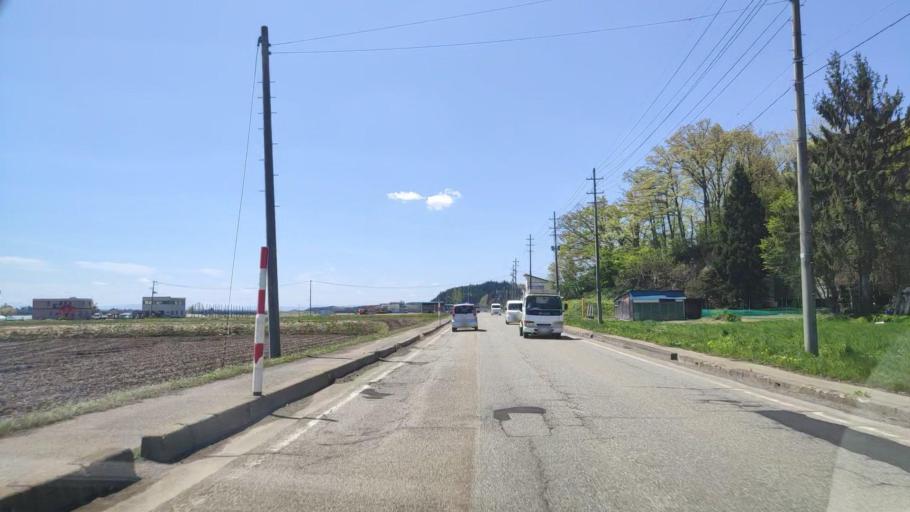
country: JP
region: Akita
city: Omagari
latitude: 39.4396
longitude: 140.4483
